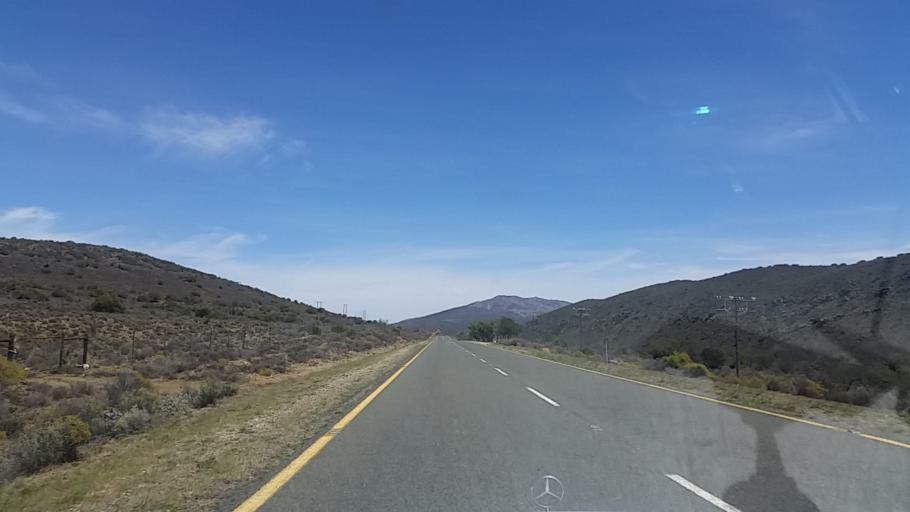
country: ZA
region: Eastern Cape
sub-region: Cacadu District Municipality
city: Willowmore
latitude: -33.3762
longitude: 23.4242
